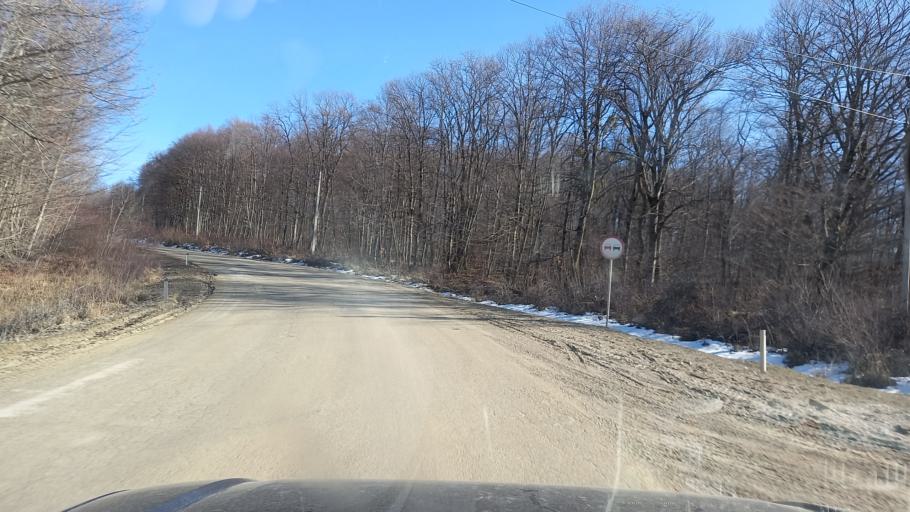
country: RU
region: Adygeya
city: Kamennomostskiy
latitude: 44.2744
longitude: 40.2783
